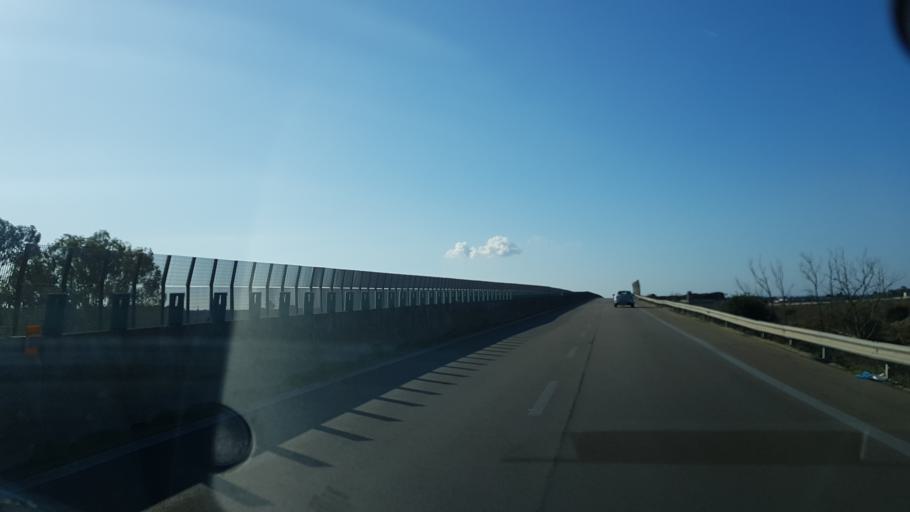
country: IT
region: Apulia
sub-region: Provincia di Lecce
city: Sannicola
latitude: 40.1148
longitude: 18.0430
